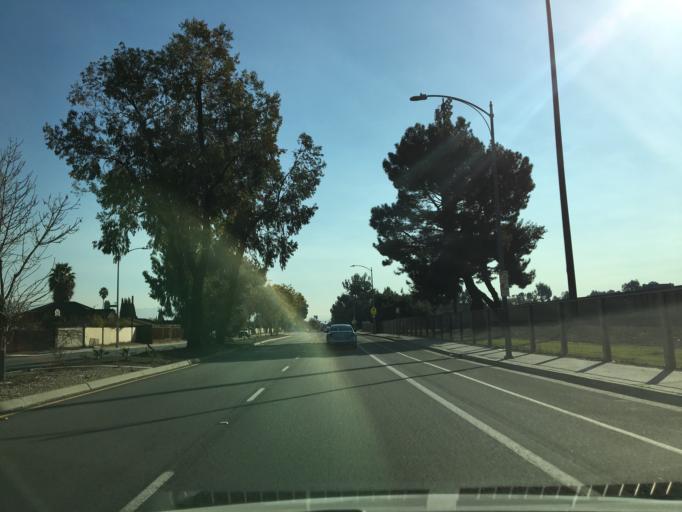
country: US
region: California
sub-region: Santa Clara County
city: Alum Rock
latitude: 37.3698
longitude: -121.8548
